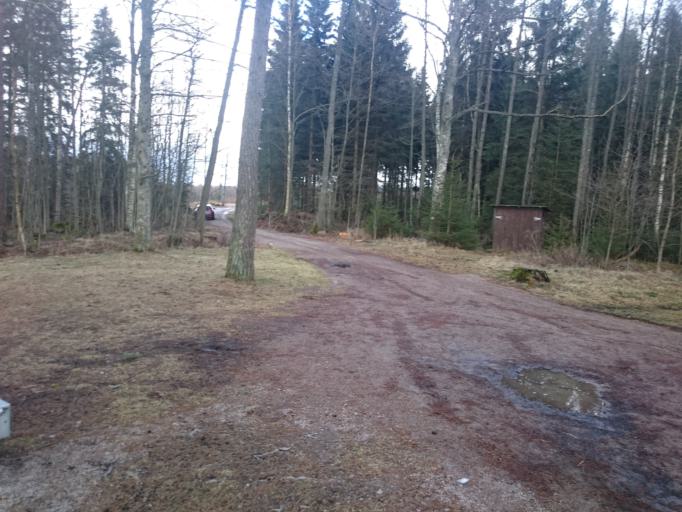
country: SE
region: Joenkoeping
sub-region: Vetlanda Kommun
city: Vetlanda
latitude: 57.3031
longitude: 15.1017
